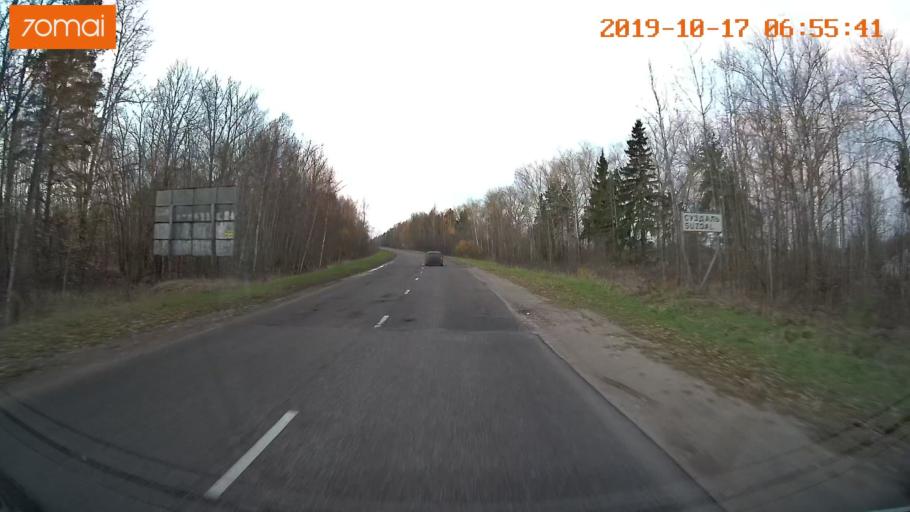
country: RU
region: Vladimir
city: Suzdal'
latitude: 56.4540
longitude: 40.4543
